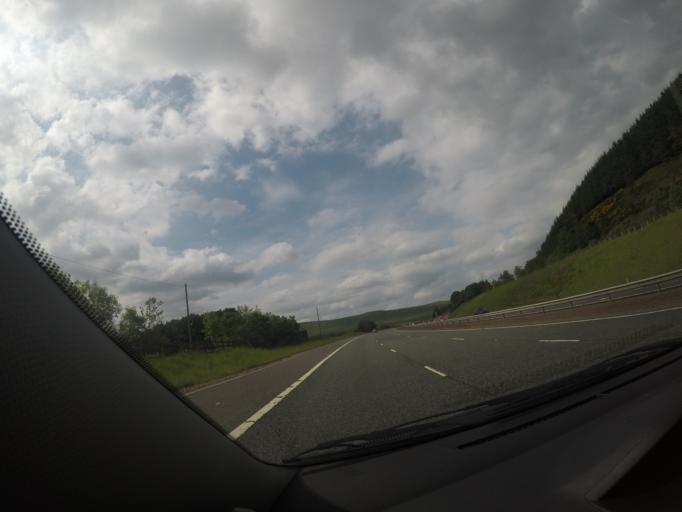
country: GB
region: Scotland
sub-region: South Lanarkshire
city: Biggar
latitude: 55.4413
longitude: -3.6517
